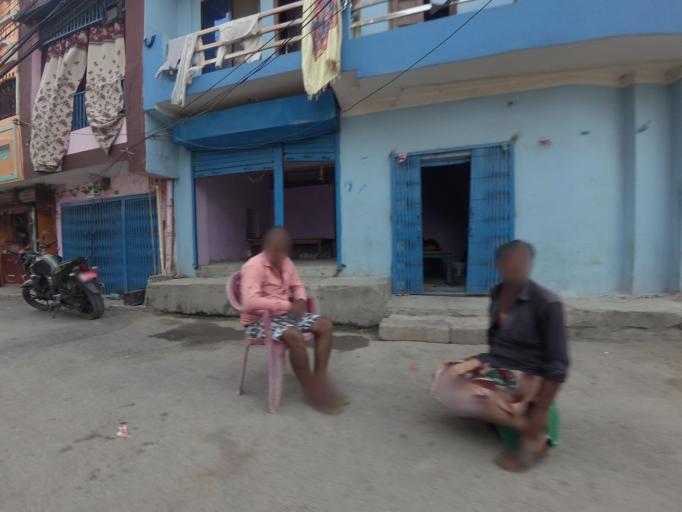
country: NP
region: Western Region
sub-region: Lumbini Zone
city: Bhairahawa
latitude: 27.5183
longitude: 83.4545
